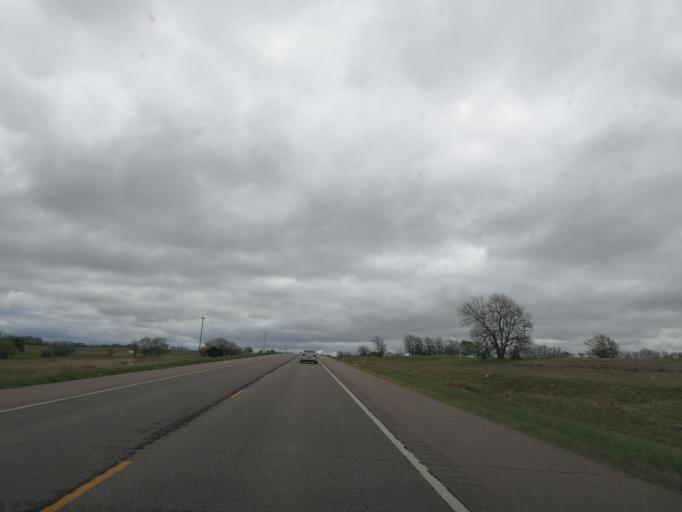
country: US
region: Kansas
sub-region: Elk County
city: Howard
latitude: 37.6362
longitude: -96.3210
